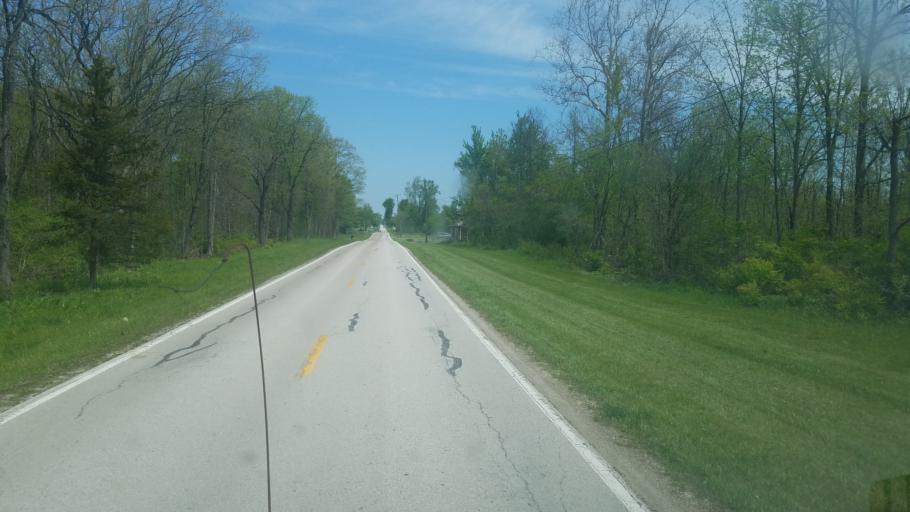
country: US
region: Ohio
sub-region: Sandusky County
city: Stony Prairie
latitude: 41.4024
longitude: -83.2023
